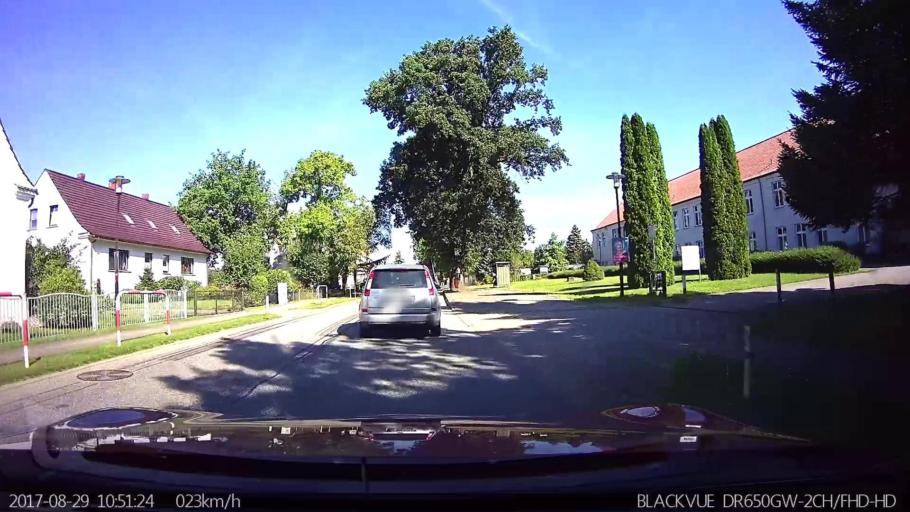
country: DE
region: Mecklenburg-Vorpommern
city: Velgast
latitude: 54.2682
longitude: 12.8129
